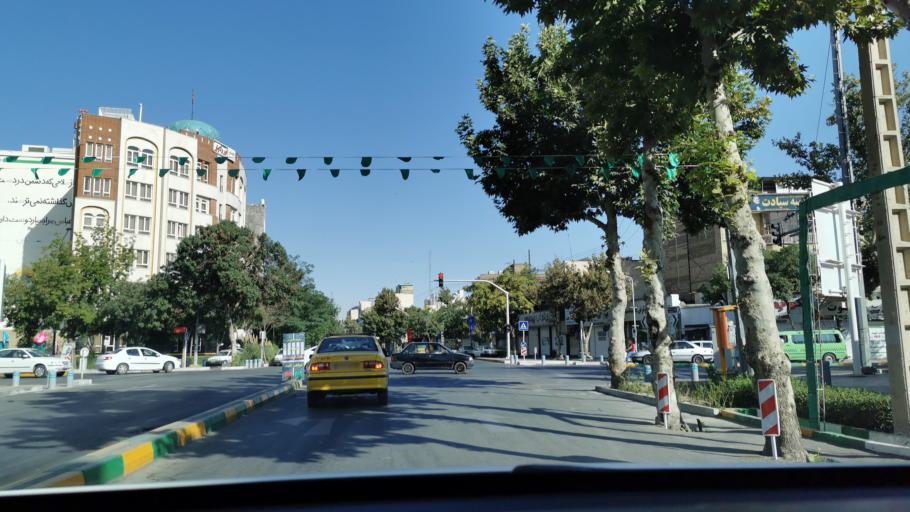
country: IR
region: Razavi Khorasan
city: Mashhad
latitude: 36.2995
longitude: 59.6182
